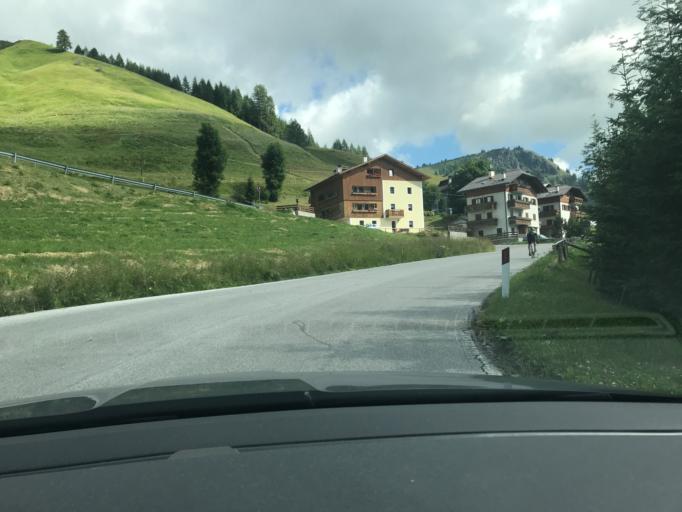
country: IT
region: Trentino-Alto Adige
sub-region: Bolzano
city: Corvara in Badia
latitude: 46.4949
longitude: 11.8666
